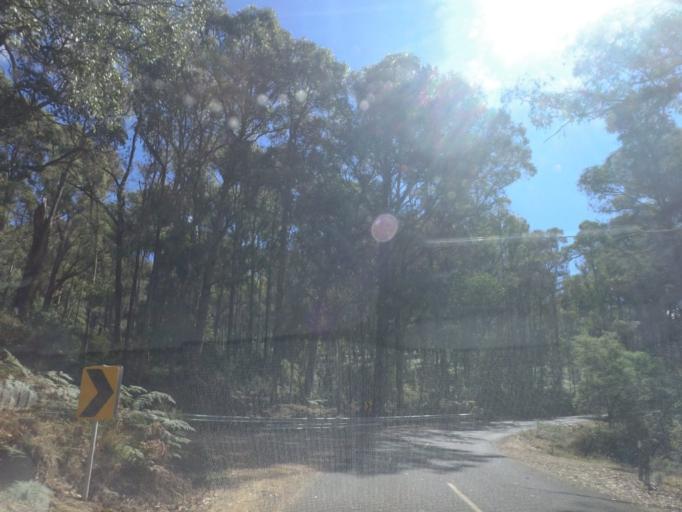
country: AU
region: Victoria
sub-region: Murrindindi
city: Alexandra
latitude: -37.3231
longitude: 145.9322
